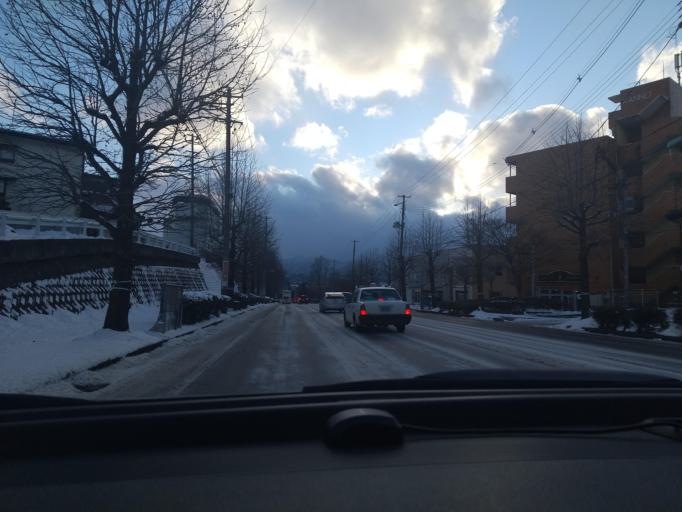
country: JP
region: Iwate
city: Morioka-shi
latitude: 39.7253
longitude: 141.1371
